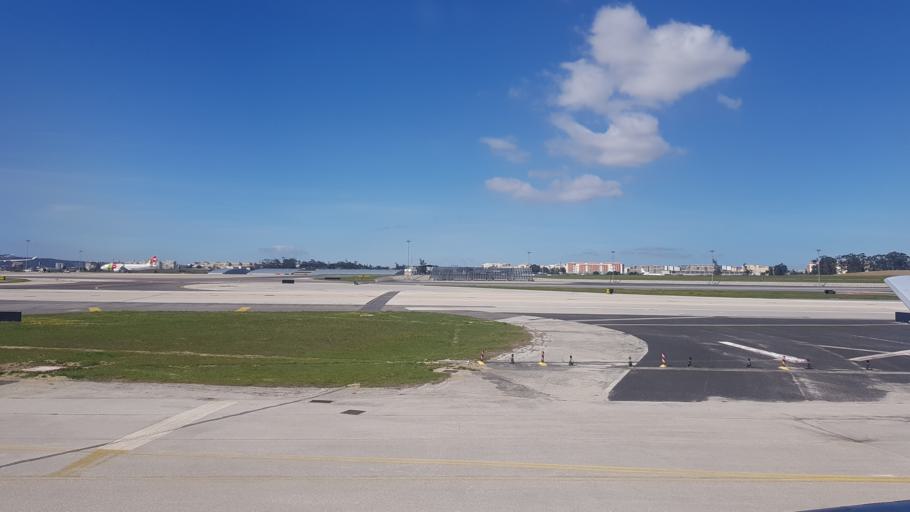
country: PT
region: Lisbon
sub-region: Loures
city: Camarate
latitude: 38.7740
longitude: -9.1328
